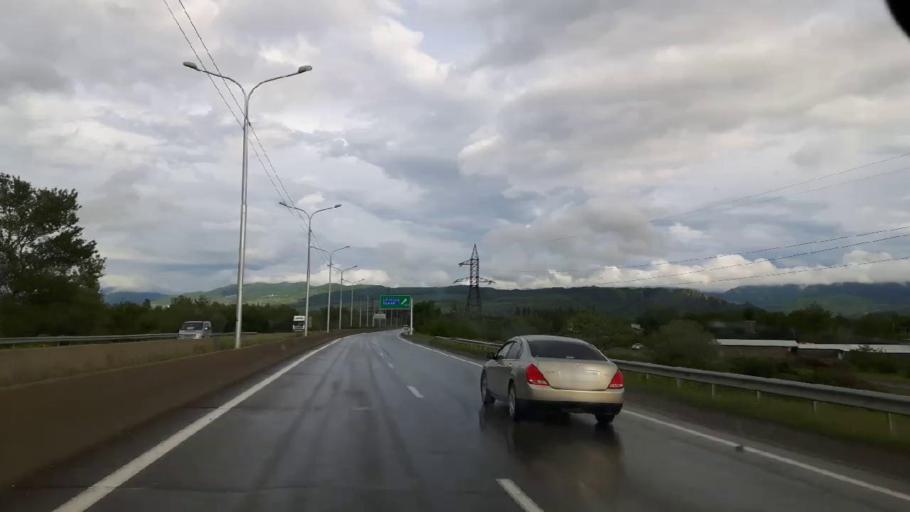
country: GE
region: Shida Kartli
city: Kaspi
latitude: 41.9174
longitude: 44.5527
